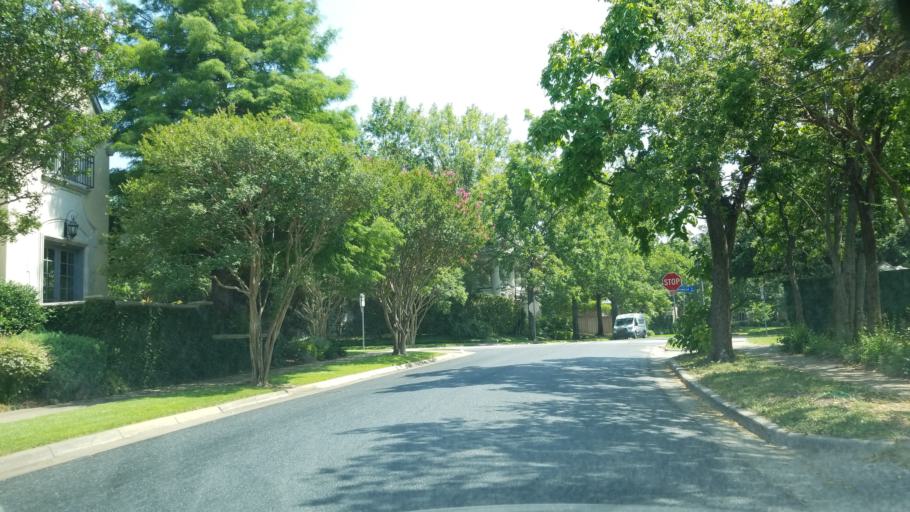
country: US
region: Texas
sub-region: Dallas County
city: Highland Park
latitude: 32.8285
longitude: -96.7911
